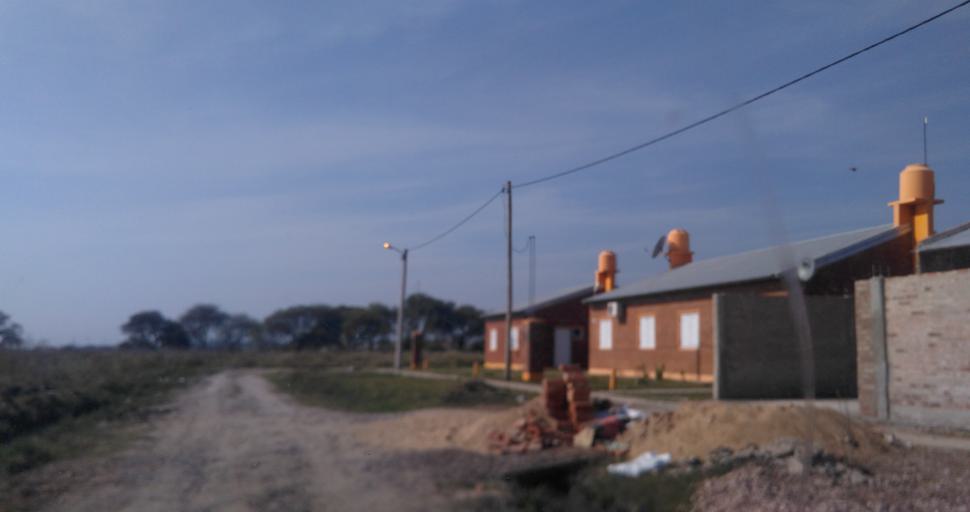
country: AR
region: Chaco
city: Fontana
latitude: -27.4542
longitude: -59.0474
